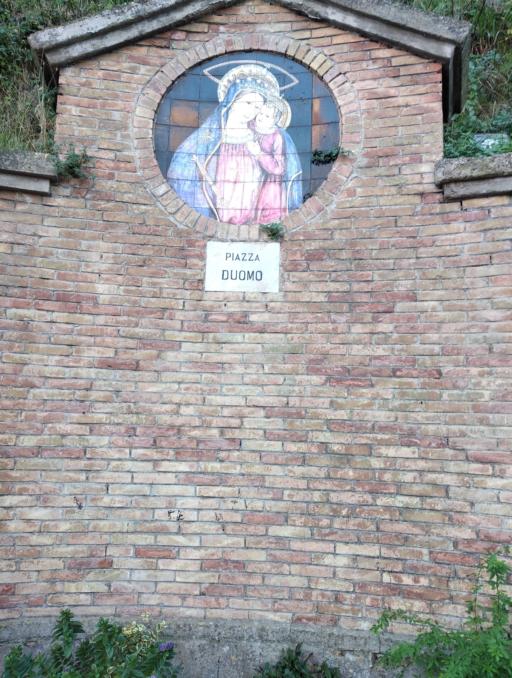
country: IT
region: Calabria
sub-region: Provincia di Cosenza
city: San Marco Argentano
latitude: 39.5588
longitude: 16.1171
